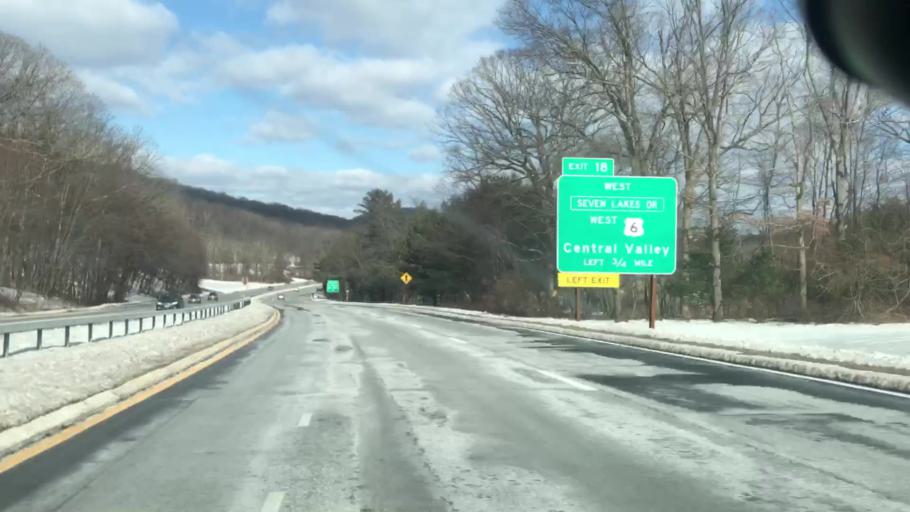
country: US
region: New York
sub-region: Orange County
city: Fort Montgomery
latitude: 41.2932
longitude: -74.0267
